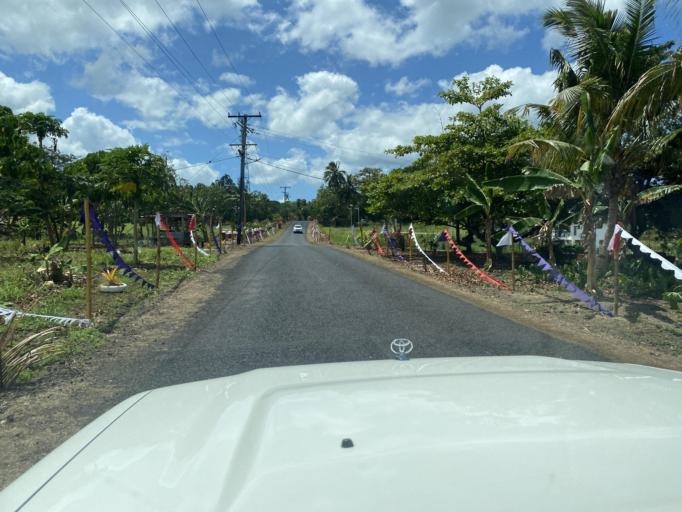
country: WS
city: Lotofaga
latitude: -14.0050
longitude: -171.7900
